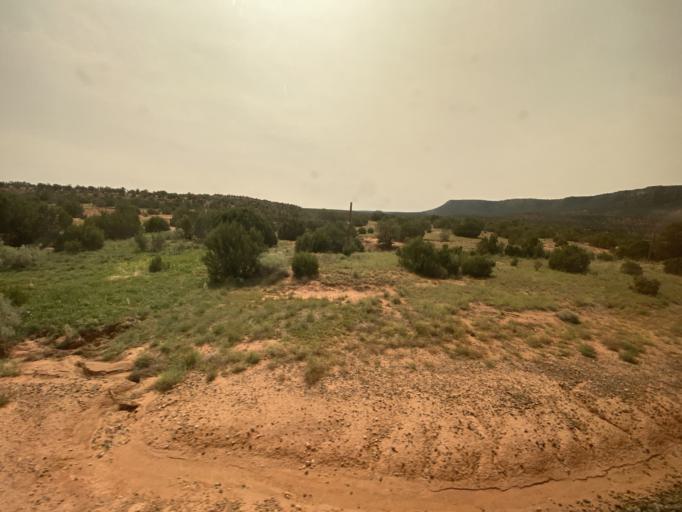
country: US
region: New Mexico
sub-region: San Miguel County
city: Pecos
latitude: 35.3922
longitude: -105.4821
